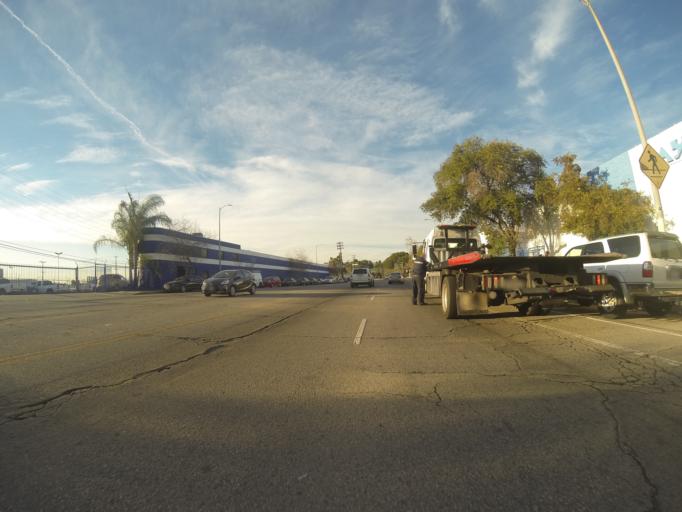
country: US
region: California
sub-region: Los Angeles County
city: San Fernando
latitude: 34.2548
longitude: -118.3927
